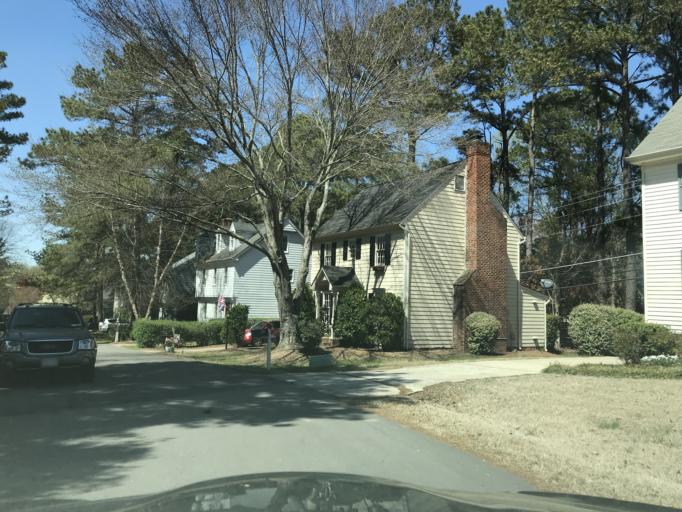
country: US
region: North Carolina
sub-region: Wake County
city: Raleigh
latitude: 35.8182
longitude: -78.5833
